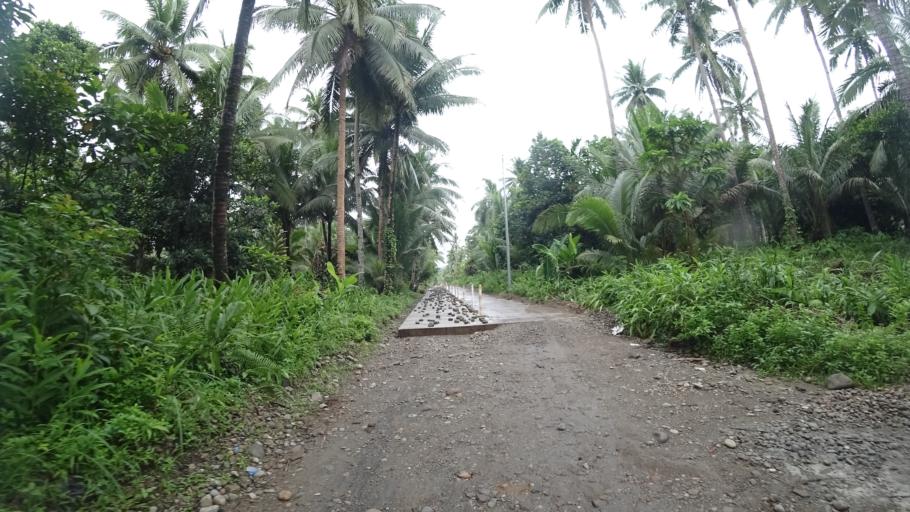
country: PH
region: Eastern Visayas
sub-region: Province of Leyte
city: Bugho
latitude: 10.8265
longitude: 124.9191
